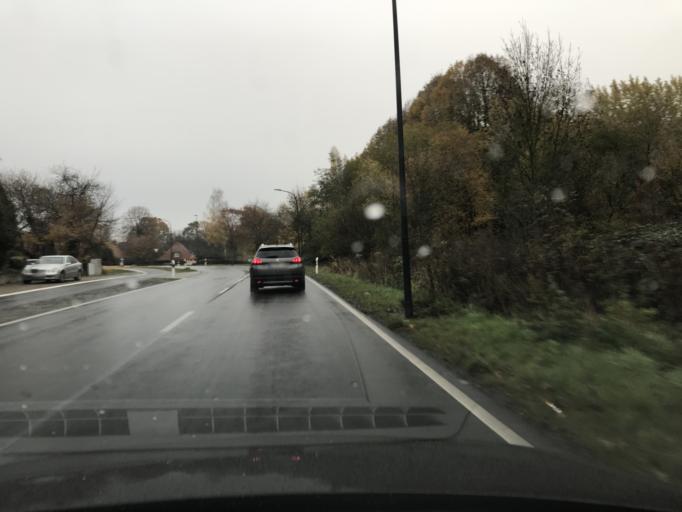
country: DE
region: North Rhine-Westphalia
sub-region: Regierungsbezirk Arnsberg
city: Hamm
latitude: 51.7049
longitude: 7.8138
